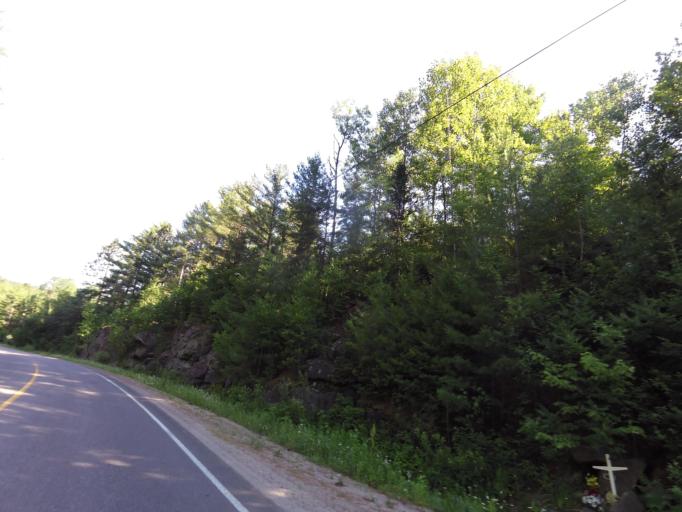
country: CA
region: Ontario
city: Deep River
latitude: 46.1904
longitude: -77.6811
